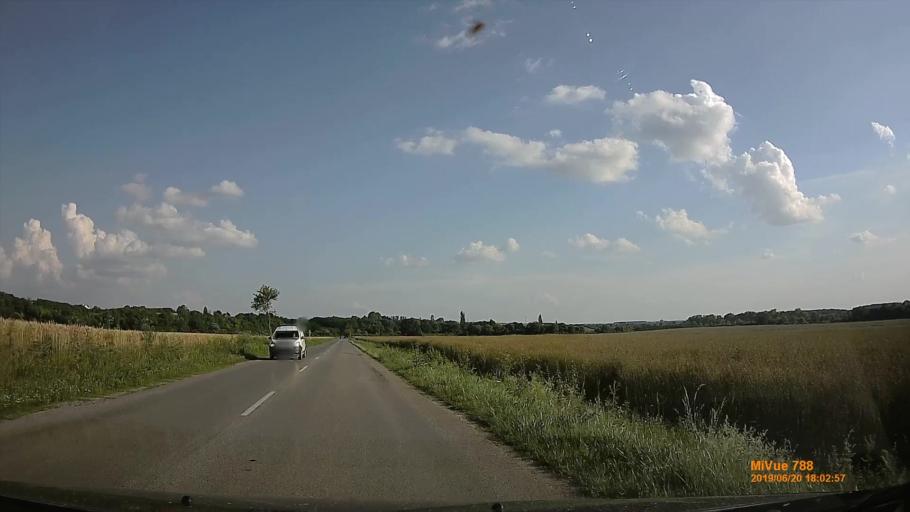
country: HU
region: Baranya
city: Szentlorinc
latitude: 46.0682
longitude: 17.9907
